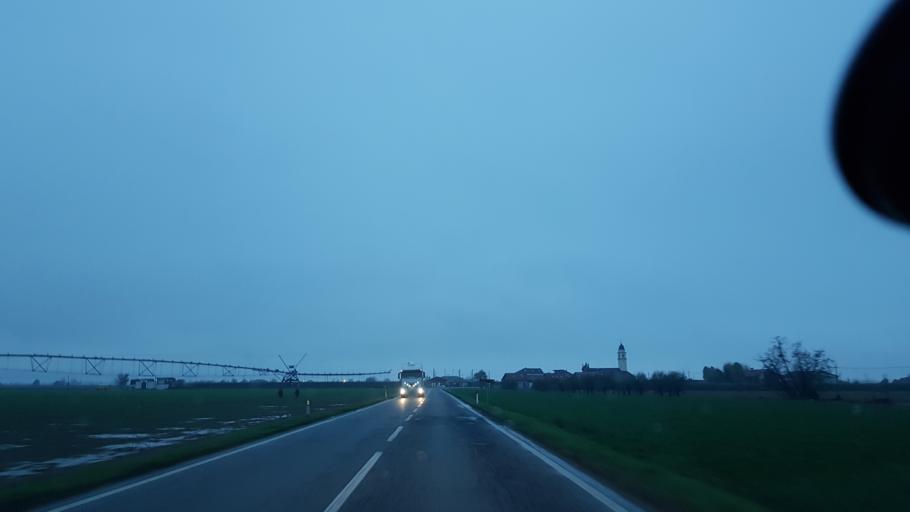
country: IT
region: Piedmont
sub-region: Provincia di Cuneo
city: Genola
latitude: 44.5570
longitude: 7.6615
